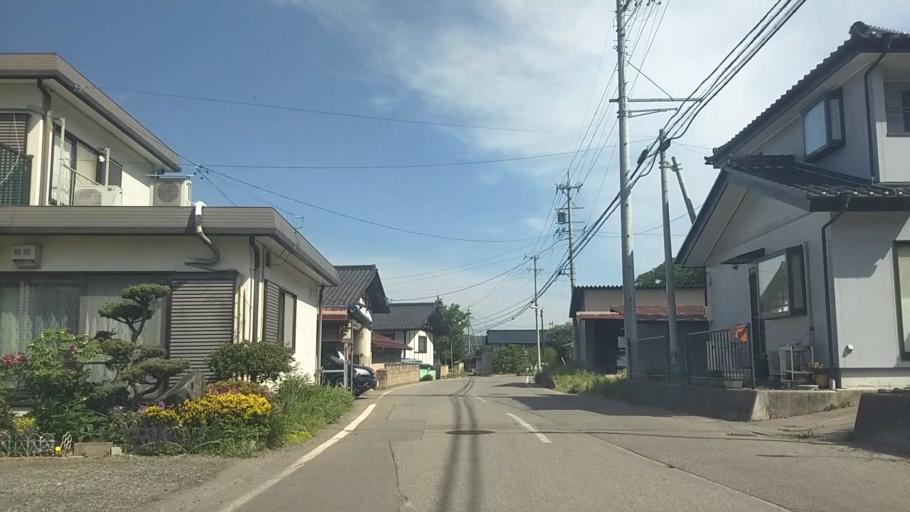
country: JP
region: Nagano
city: Saku
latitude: 36.1122
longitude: 138.4784
